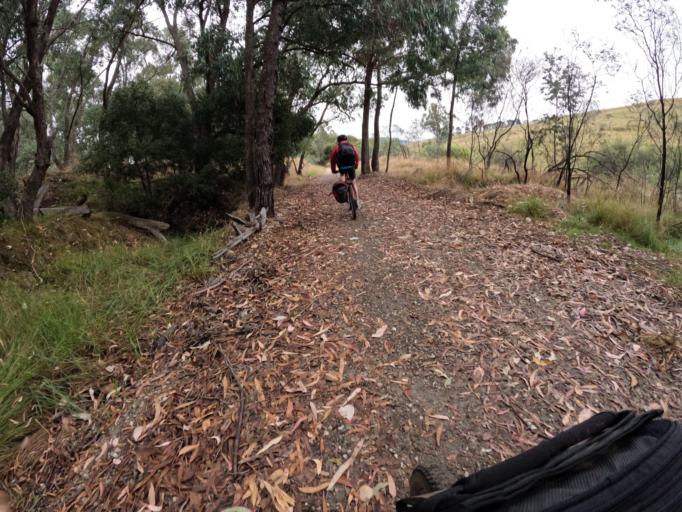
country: AU
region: New South Wales
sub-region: Greater Hume Shire
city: Holbrook
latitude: -36.1627
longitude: 147.4074
